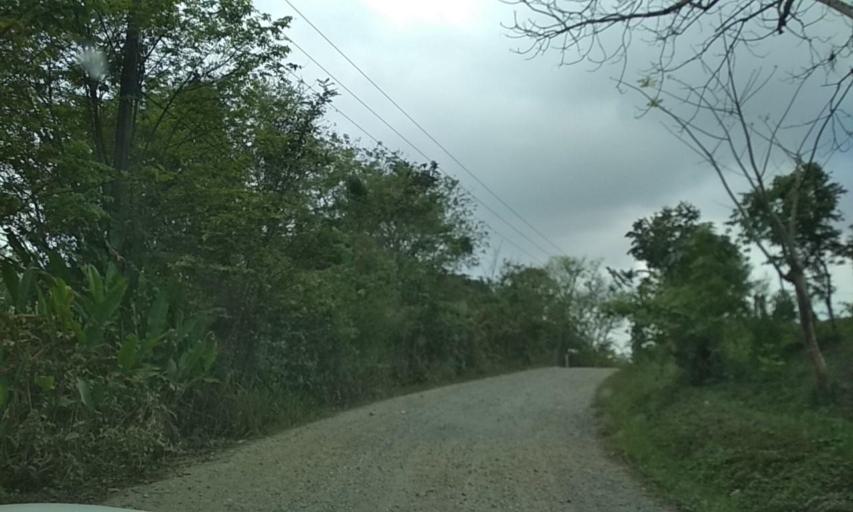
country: MX
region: Veracruz
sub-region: Uxpanapa
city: Poblado 10
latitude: 17.5034
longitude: -94.1583
